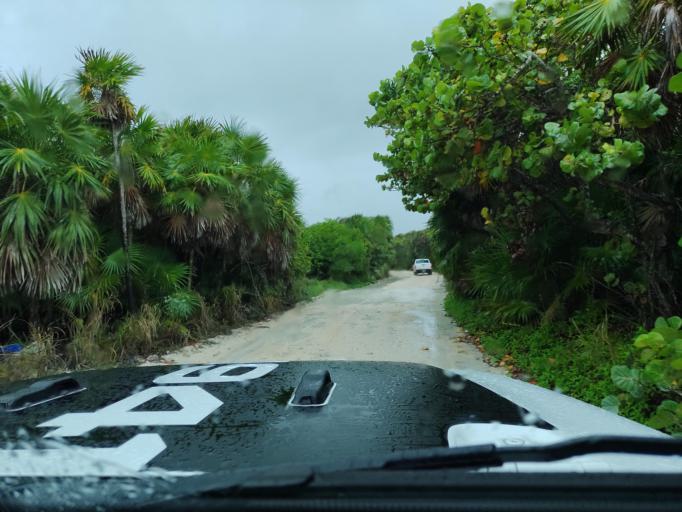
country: MX
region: Quintana Roo
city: Tulum
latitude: 19.9809
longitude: -87.4684
